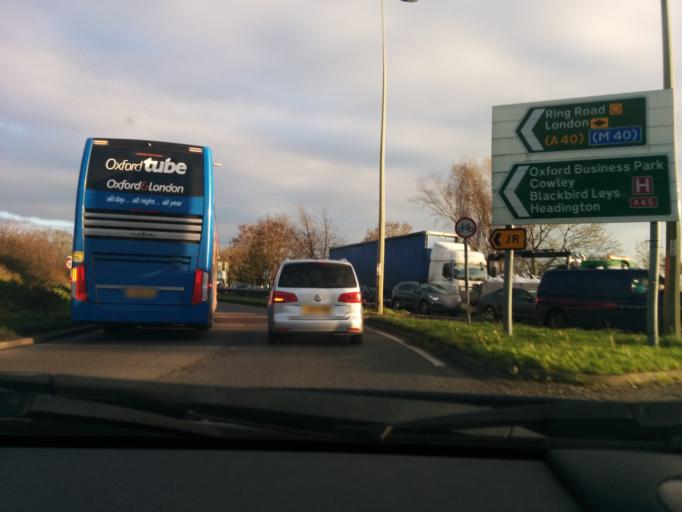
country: GB
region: England
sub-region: Oxfordshire
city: Cowley
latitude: 51.7247
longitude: -1.2237
